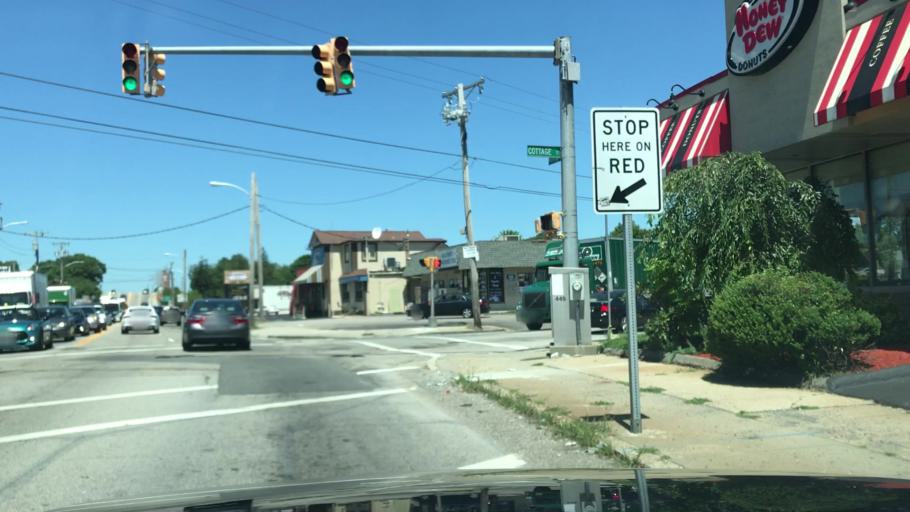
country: US
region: Massachusetts
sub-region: Bristol County
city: North Seekonk
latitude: 41.8941
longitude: -71.3540
